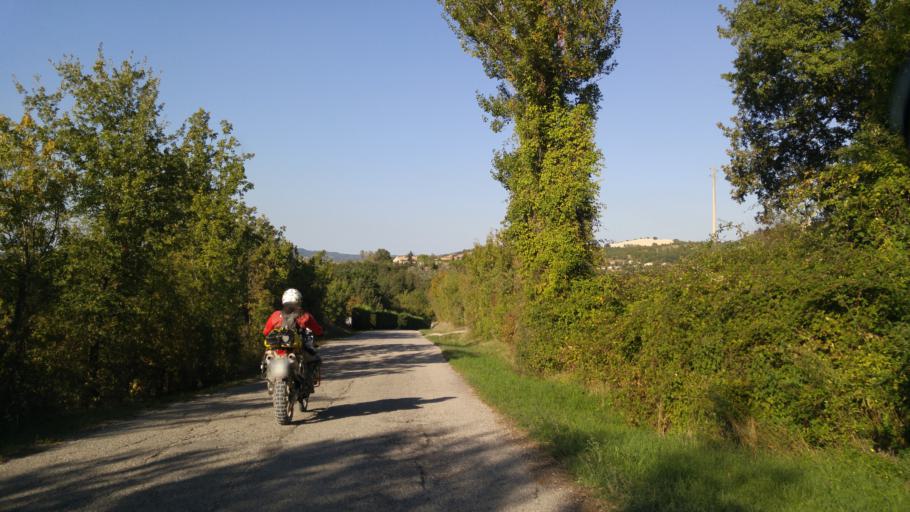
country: IT
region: The Marches
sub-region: Provincia di Pesaro e Urbino
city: Fermignano
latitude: 43.6594
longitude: 12.6498
